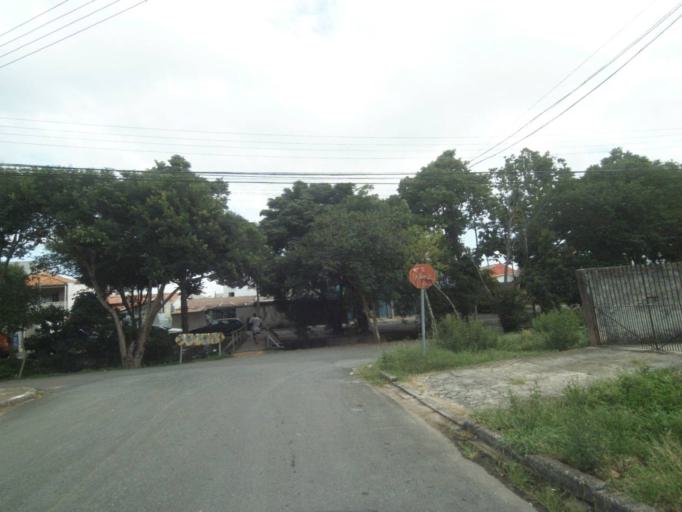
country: BR
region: Parana
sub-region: Pinhais
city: Pinhais
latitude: -25.4544
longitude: -49.2040
